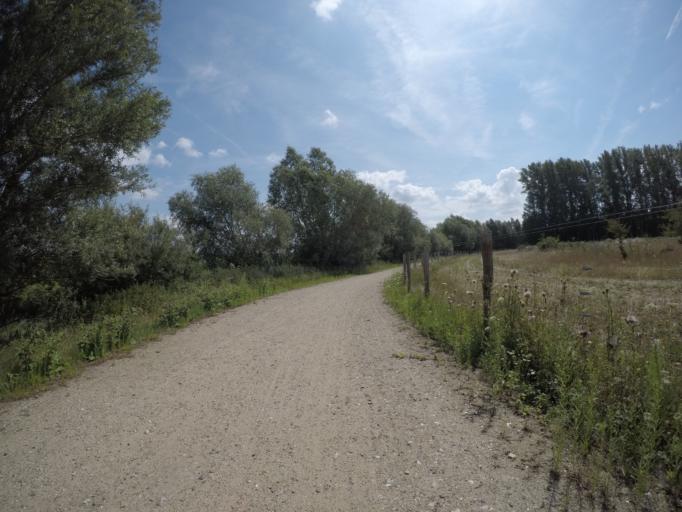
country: DE
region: North Rhine-Westphalia
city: Rees
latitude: 51.7683
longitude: 6.4439
